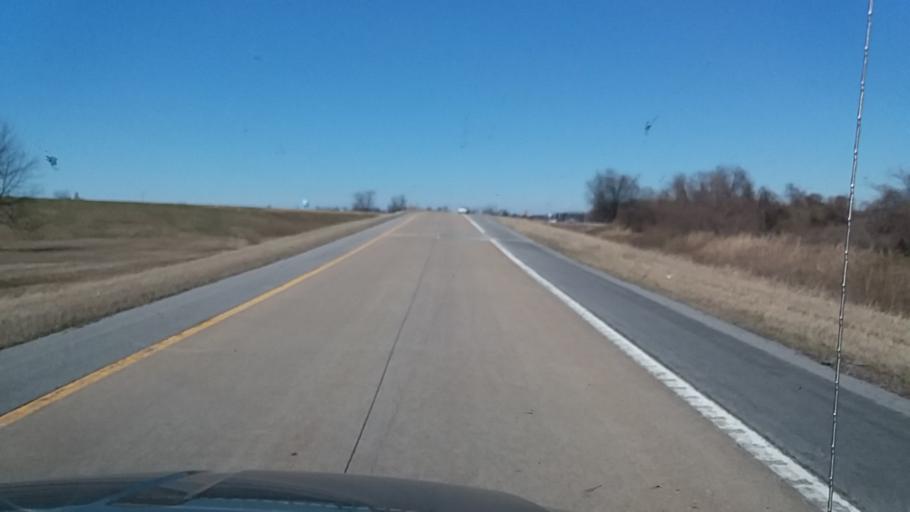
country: US
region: Missouri
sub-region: Pemiscot County
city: Hayti
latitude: 36.2172
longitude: -89.7445
